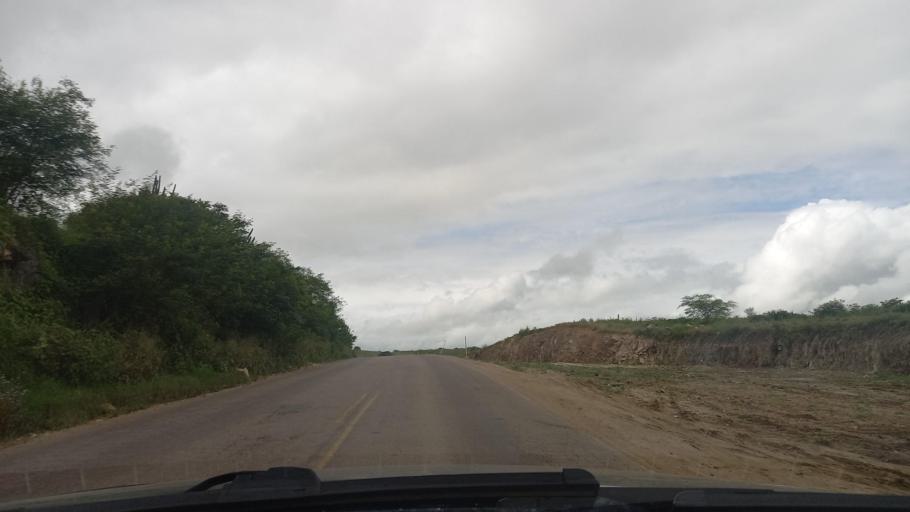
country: BR
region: Alagoas
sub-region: Batalha
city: Batalha
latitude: -9.6407
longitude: -37.1946
